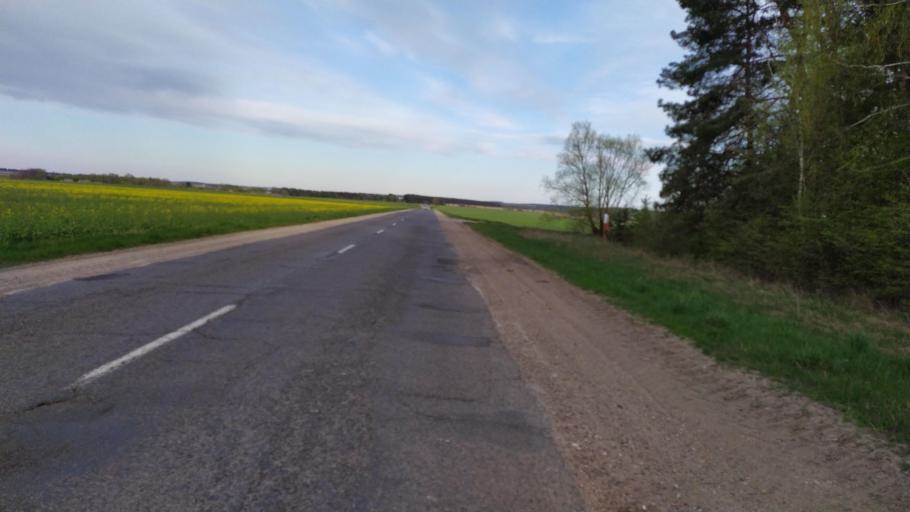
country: BY
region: Brest
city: Kamyanyets
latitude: 52.4147
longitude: 23.7087
